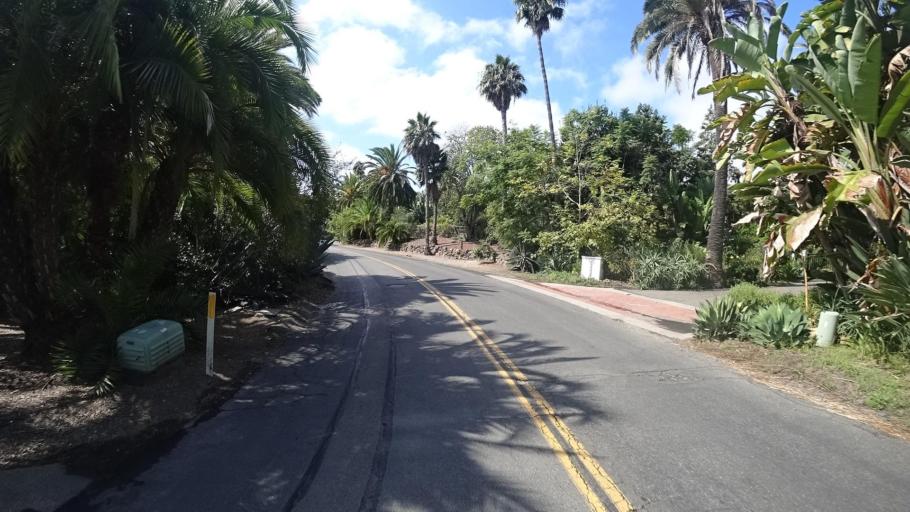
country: US
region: California
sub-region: San Diego County
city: Rancho Santa Fe
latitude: 33.0289
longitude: -117.2016
